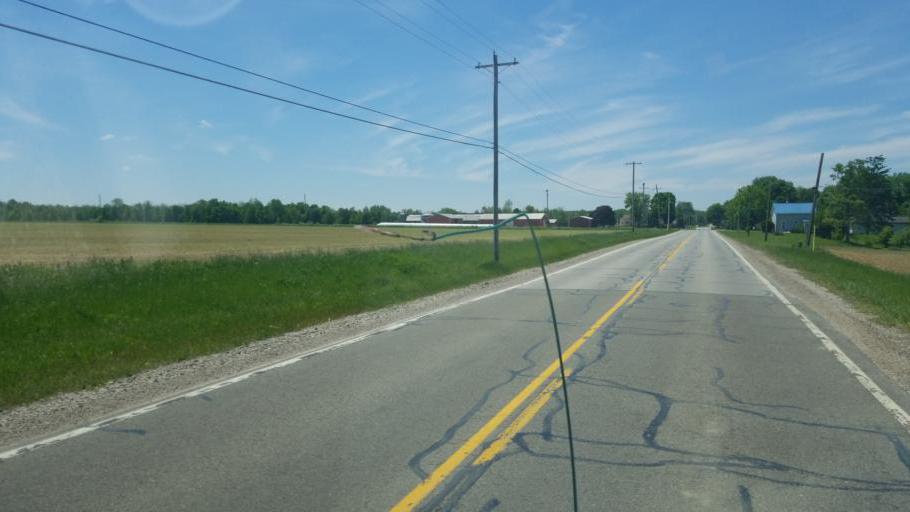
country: US
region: Ohio
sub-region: Huron County
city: Greenwich
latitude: 41.0301
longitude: -82.5331
